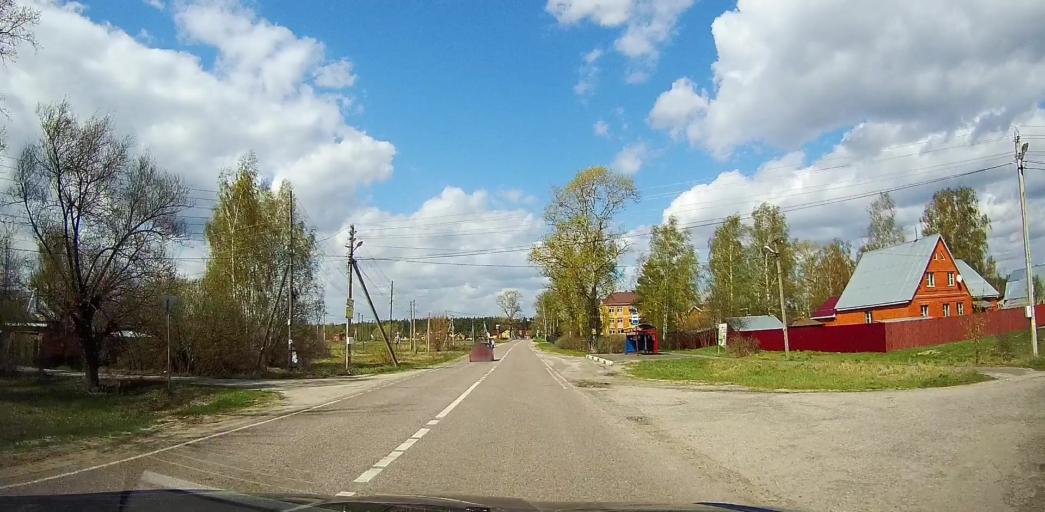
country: RU
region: Moskovskaya
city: Davydovo
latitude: 55.5567
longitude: 38.8143
